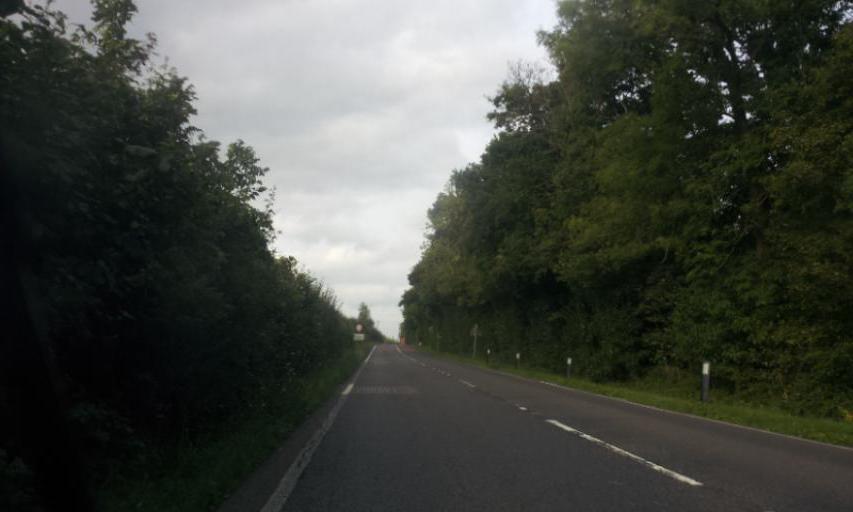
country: GB
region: England
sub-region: Kent
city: East Peckham
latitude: 51.2287
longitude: 0.4029
